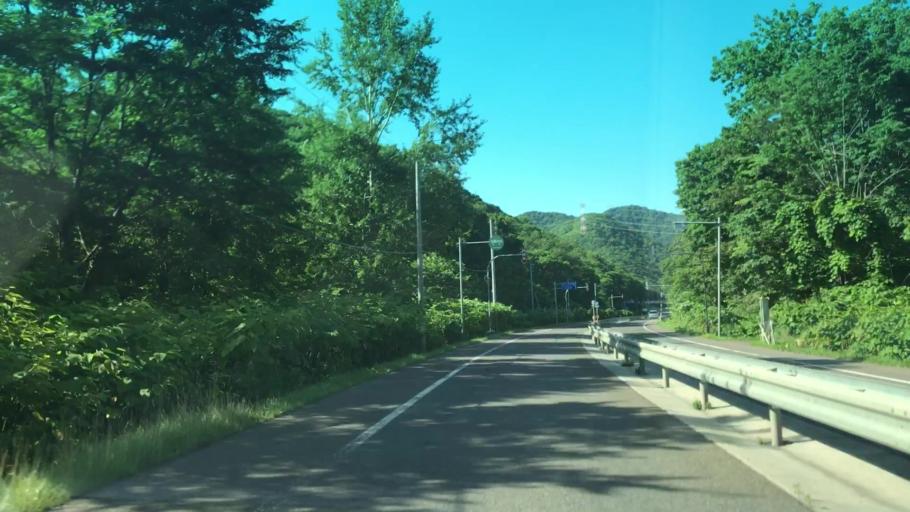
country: JP
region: Hokkaido
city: Iwanai
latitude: 43.0090
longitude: 140.6654
